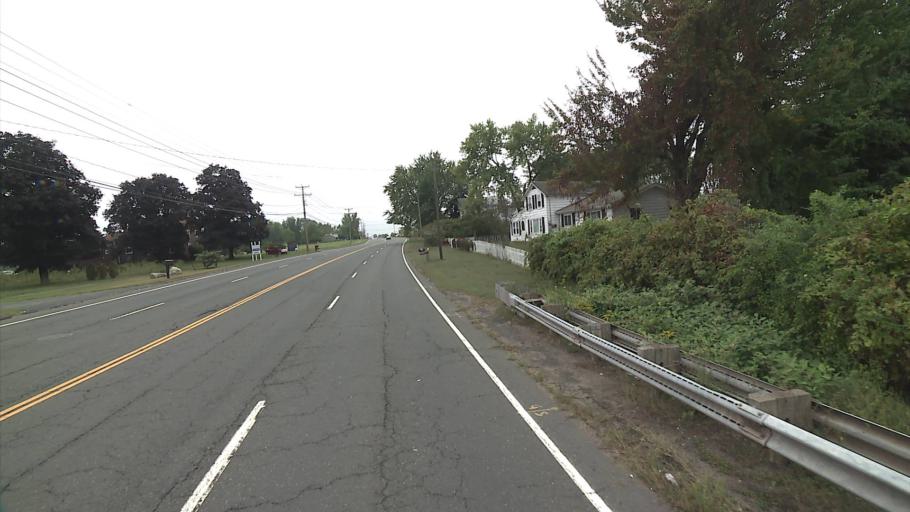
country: US
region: Connecticut
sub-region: Hartford County
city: Suffield Depot
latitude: 41.9505
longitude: -72.6666
